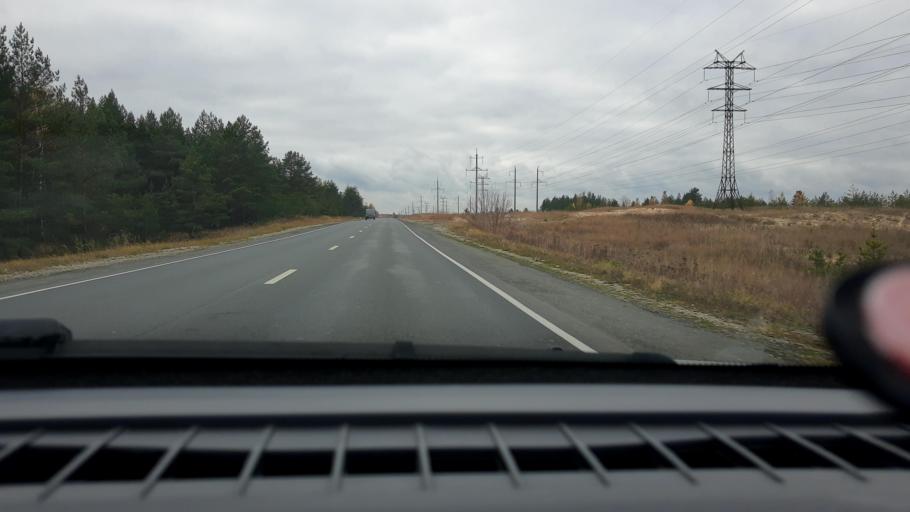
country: RU
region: Nizjnij Novgorod
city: Lukino
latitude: 56.3824
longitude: 43.6325
